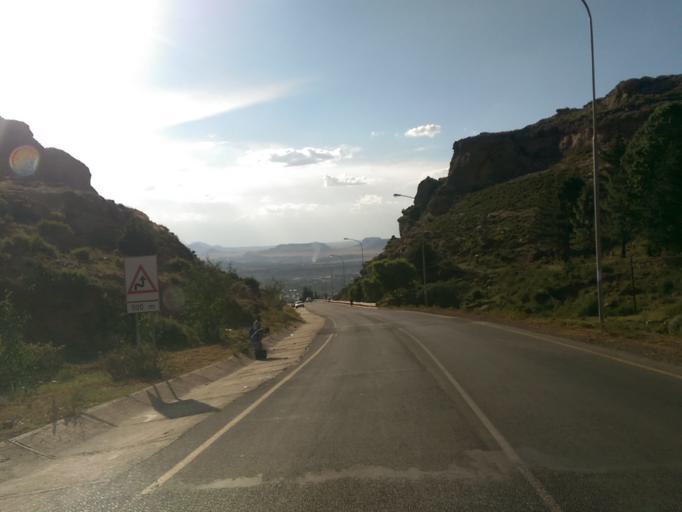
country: LS
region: Maseru
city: Maseru
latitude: -29.3154
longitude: 27.5513
